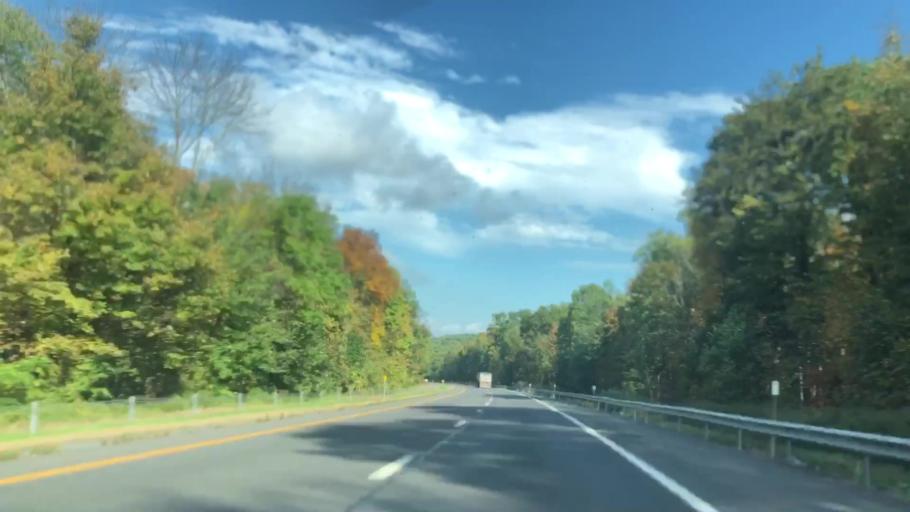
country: US
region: New York
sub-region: Ulster County
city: Tillson
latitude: 41.7861
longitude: -74.0499
